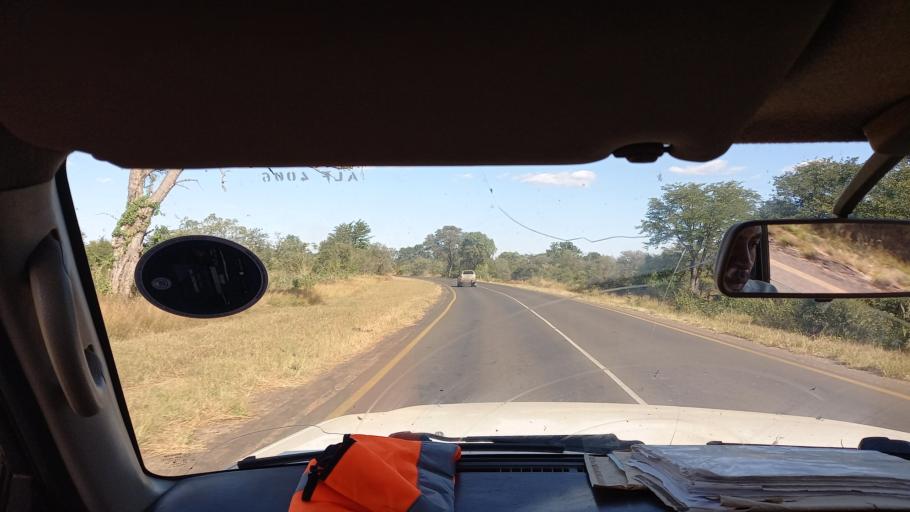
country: ZW
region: Matabeleland North
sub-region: Hwange District
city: Victoria Falls
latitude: -17.9040
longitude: 25.8560
